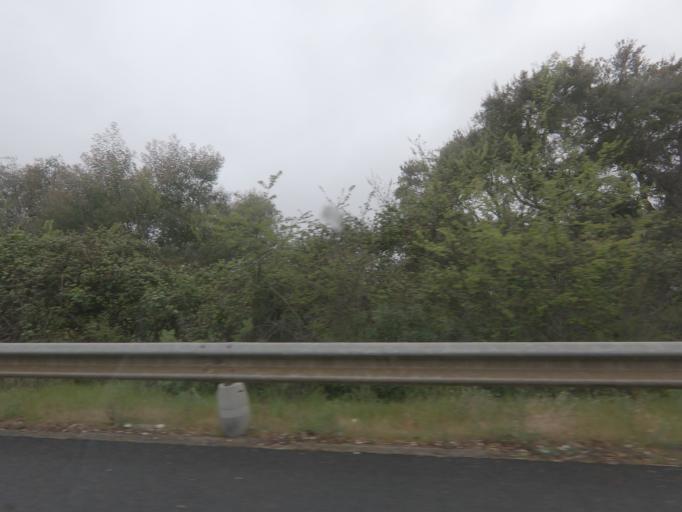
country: ES
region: Extremadura
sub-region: Provincia de Badajoz
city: Puebla de Obando
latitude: 39.1716
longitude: -6.6262
